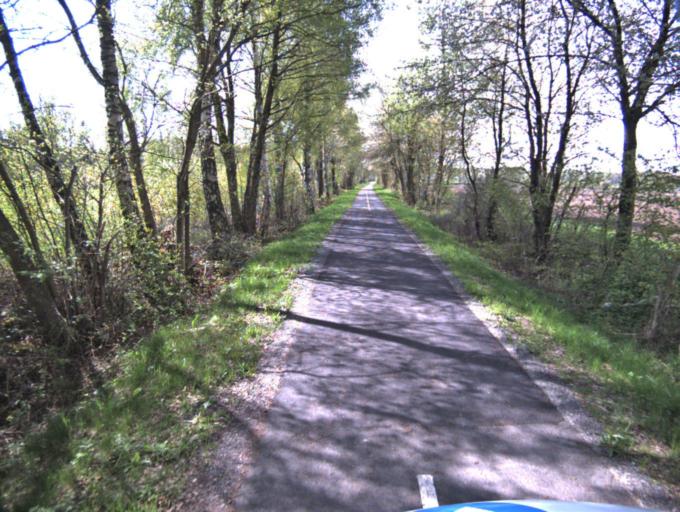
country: SE
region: Skane
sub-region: Kristianstads Kommun
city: Onnestad
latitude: 56.0035
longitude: 14.0476
